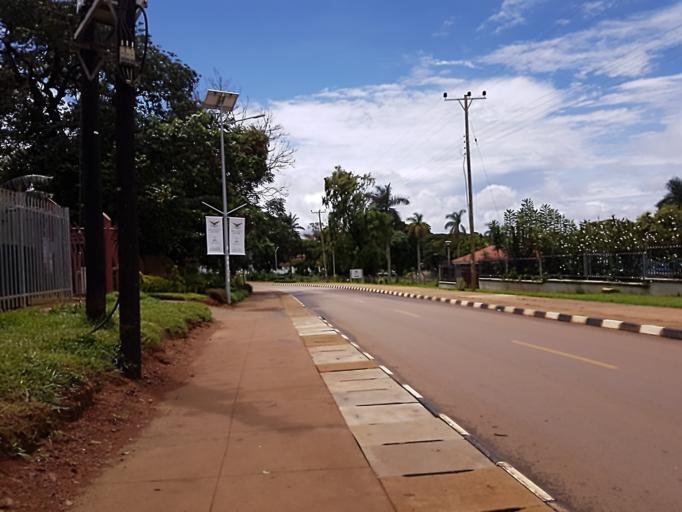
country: UG
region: Central Region
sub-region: Wakiso District
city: Entebbe
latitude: 0.0527
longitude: 32.4659
